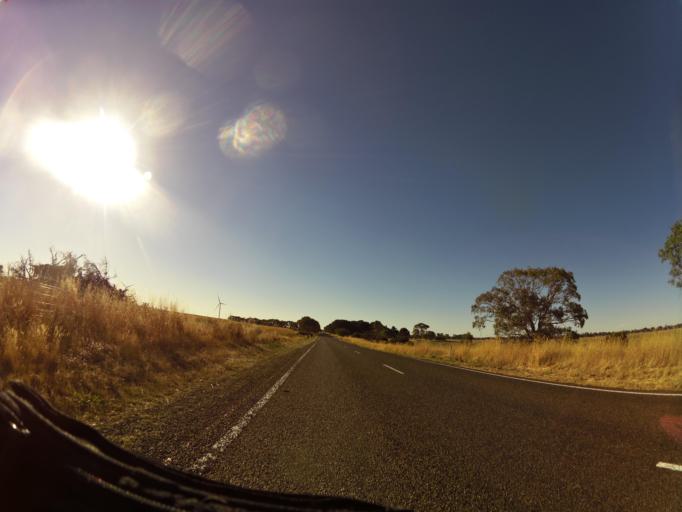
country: AU
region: Victoria
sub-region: Ballarat North
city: Delacombe
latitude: -37.5278
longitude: 143.3686
